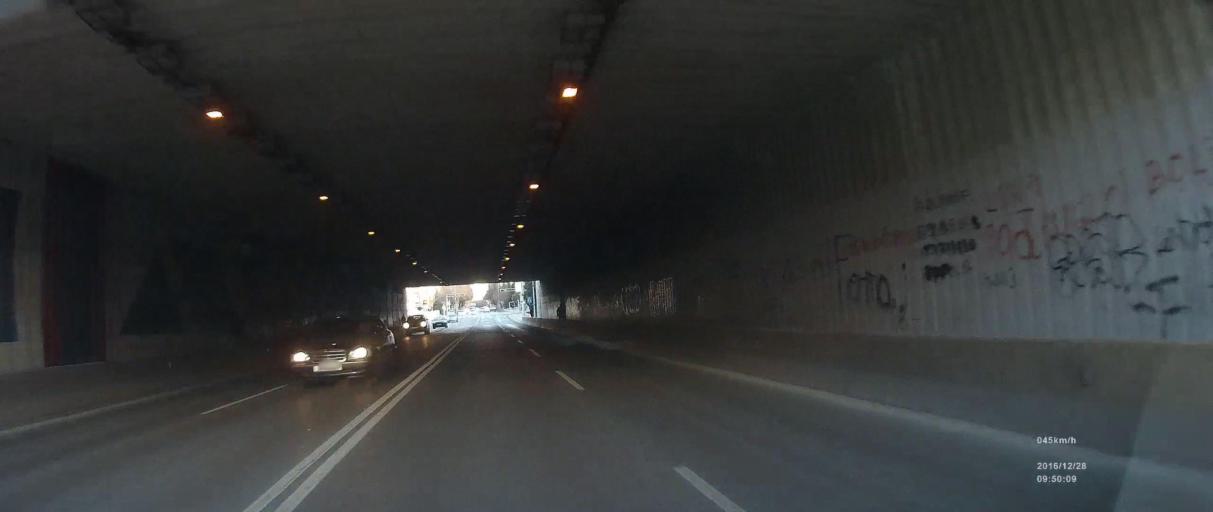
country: HR
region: Splitsko-Dalmatinska
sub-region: Grad Split
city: Split
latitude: 43.5075
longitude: 16.4557
